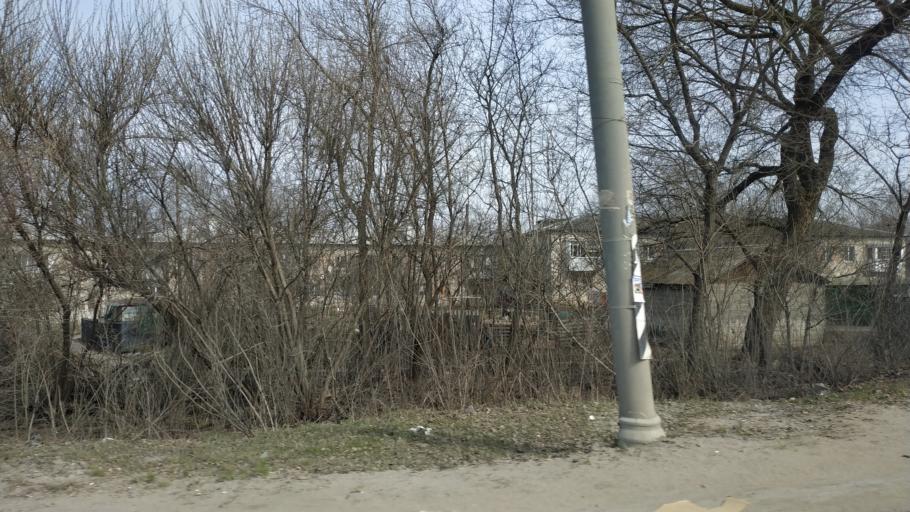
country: RU
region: Moskovskaya
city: Bronnitsy
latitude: 55.4048
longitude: 38.3017
